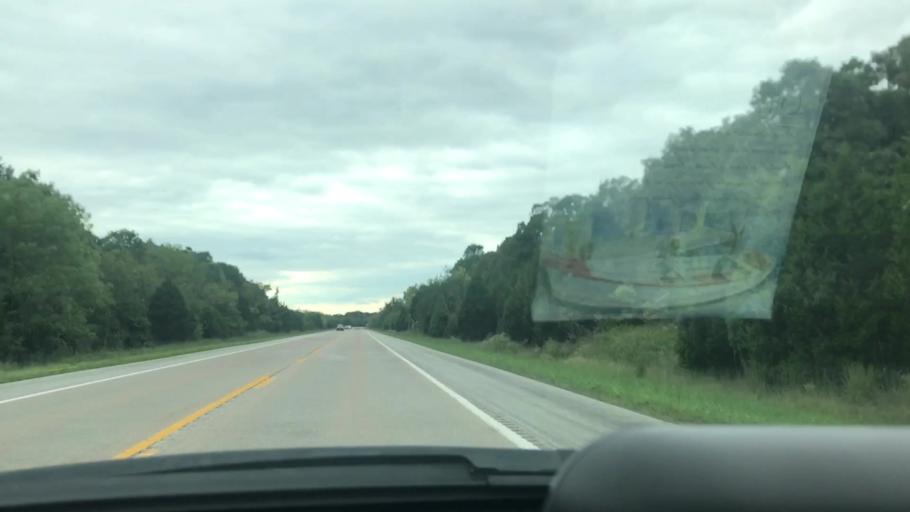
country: US
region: Missouri
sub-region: Benton County
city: Warsaw
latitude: 38.2095
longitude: -93.3341
